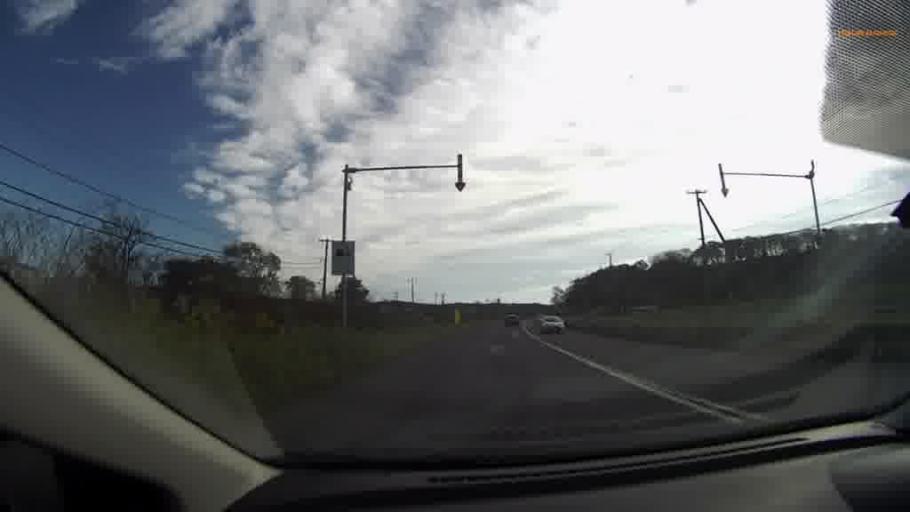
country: JP
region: Hokkaido
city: Kushiro
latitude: 42.9559
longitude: 144.0596
